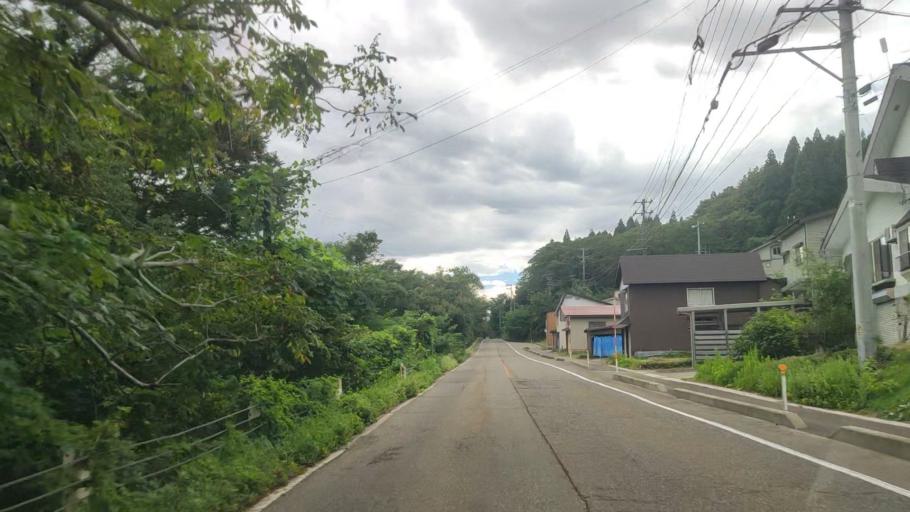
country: JP
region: Niigata
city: Arai
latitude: 36.9985
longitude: 138.2667
